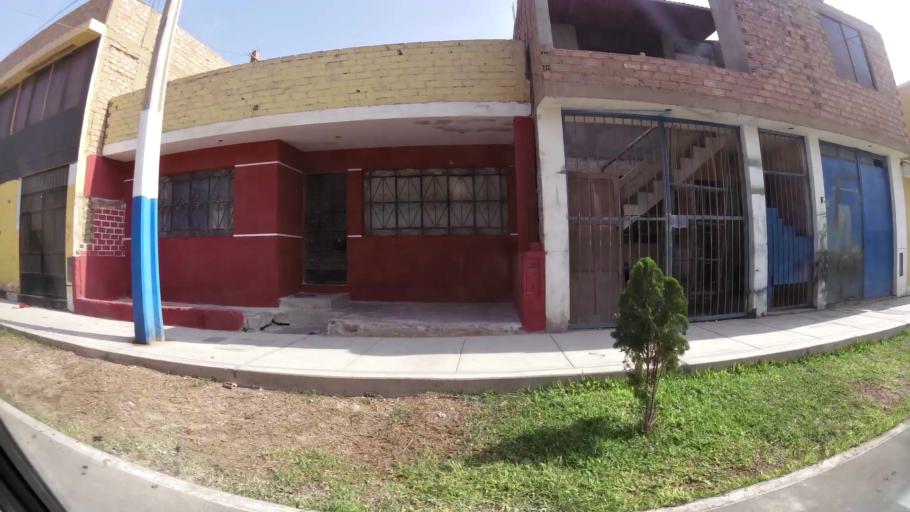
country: PE
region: Lima
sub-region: Lima
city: Santa Rosa
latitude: -11.7822
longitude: -77.1610
